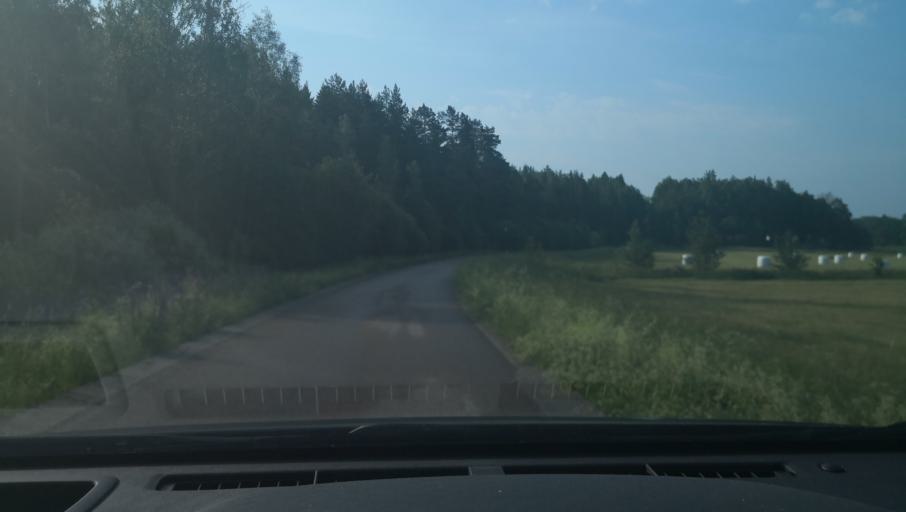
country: SE
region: Vaestmanland
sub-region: Arboga Kommun
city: Tyringe
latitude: 59.3920
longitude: 15.9429
